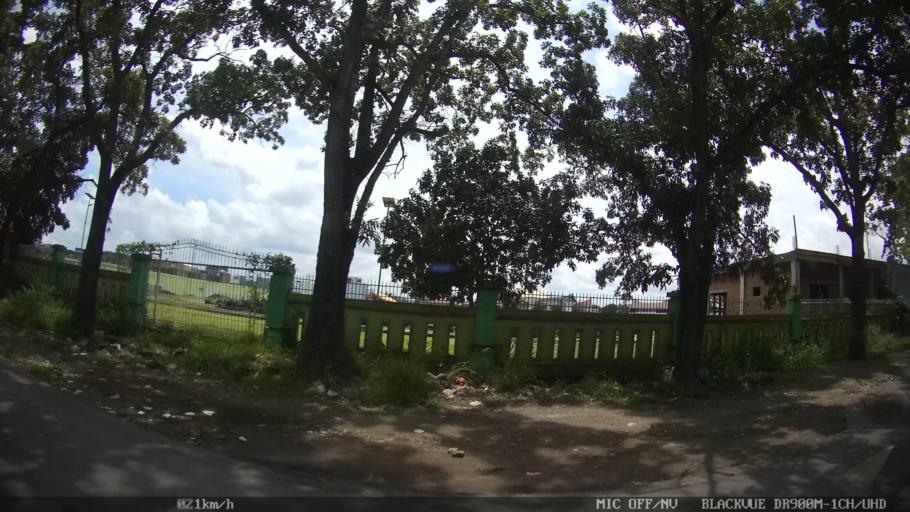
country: ID
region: North Sumatra
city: Medan
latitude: 3.6142
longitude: 98.7102
